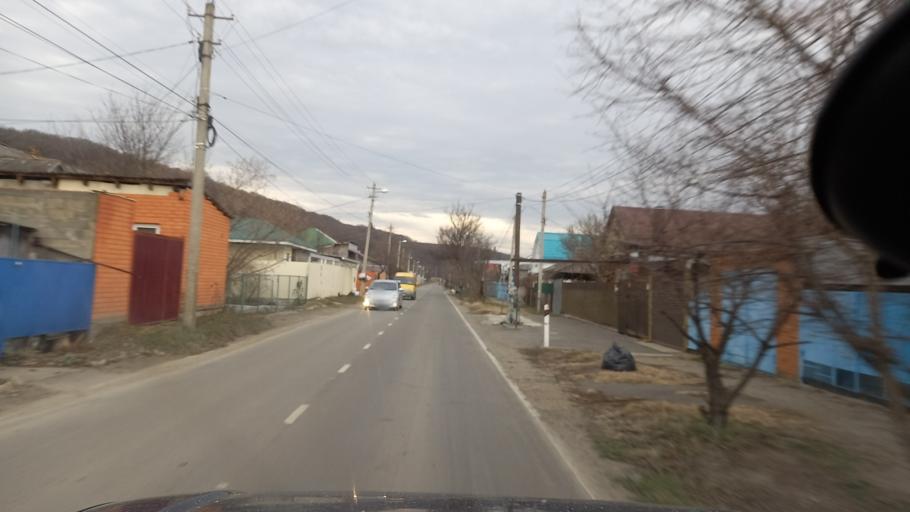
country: RU
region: Adygeya
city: Maykop
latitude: 44.5920
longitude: 40.1016
